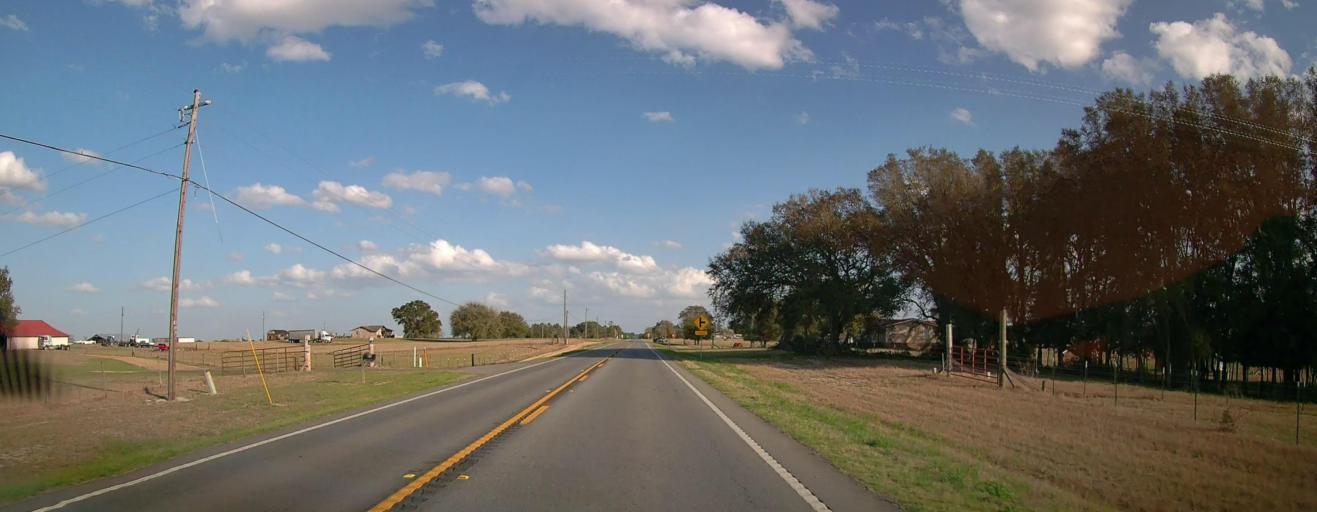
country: US
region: Georgia
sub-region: Tattnall County
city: Reidsville
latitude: 32.1028
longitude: -82.1664
